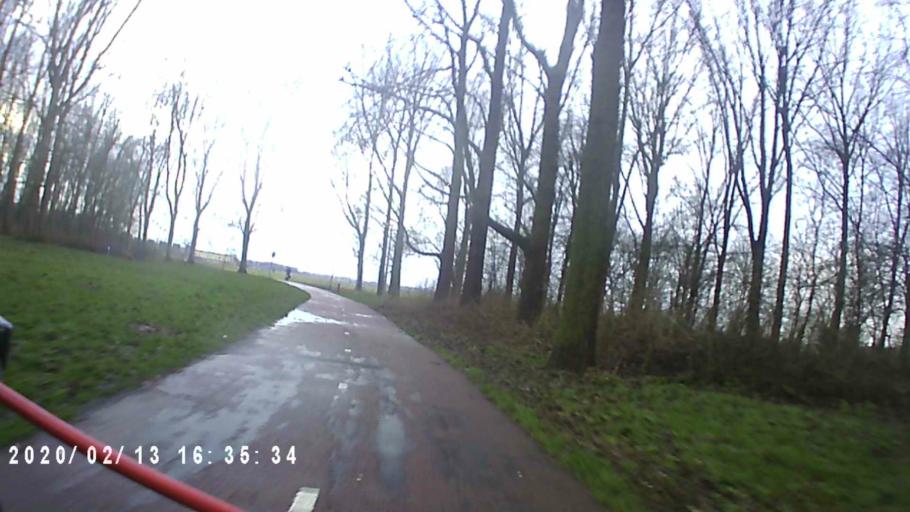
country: NL
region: Groningen
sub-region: Gemeente Groningen
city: Korrewegwijk
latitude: 53.2315
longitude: 6.5205
